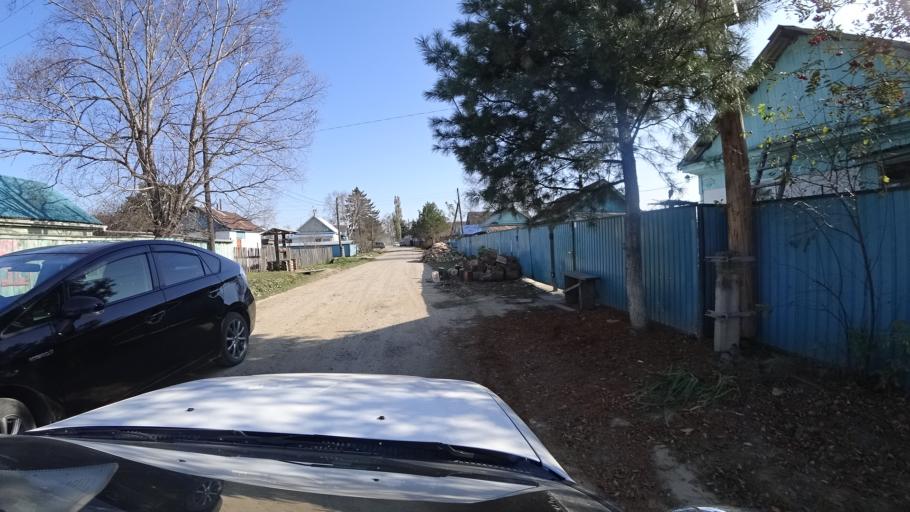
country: RU
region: Primorskiy
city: Dal'nerechensk
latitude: 45.9270
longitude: 133.7177
